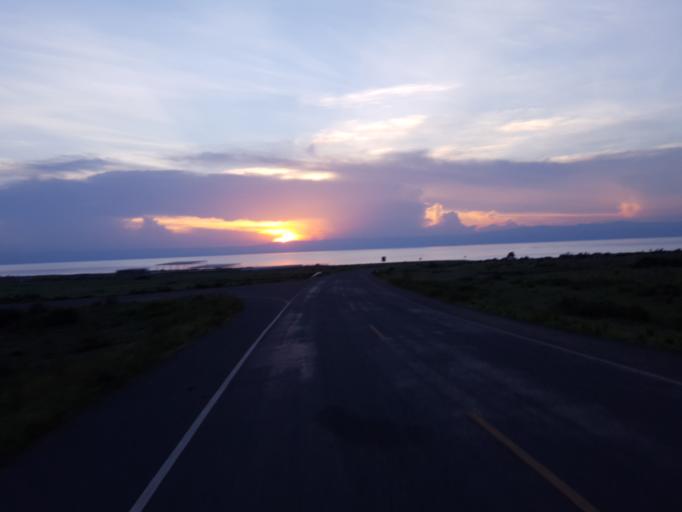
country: UG
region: Western Region
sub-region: Kibale District
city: Kagadi
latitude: 1.2532
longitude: 30.7563
